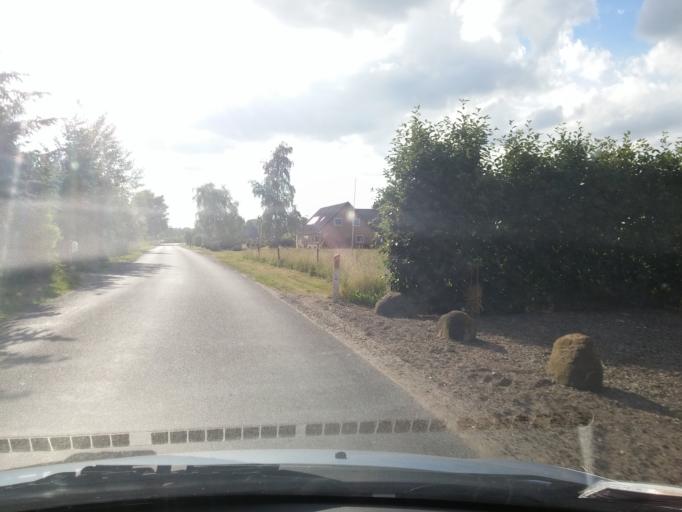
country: DK
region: South Denmark
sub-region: Kerteminde Kommune
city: Langeskov
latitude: 55.3933
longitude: 10.5639
